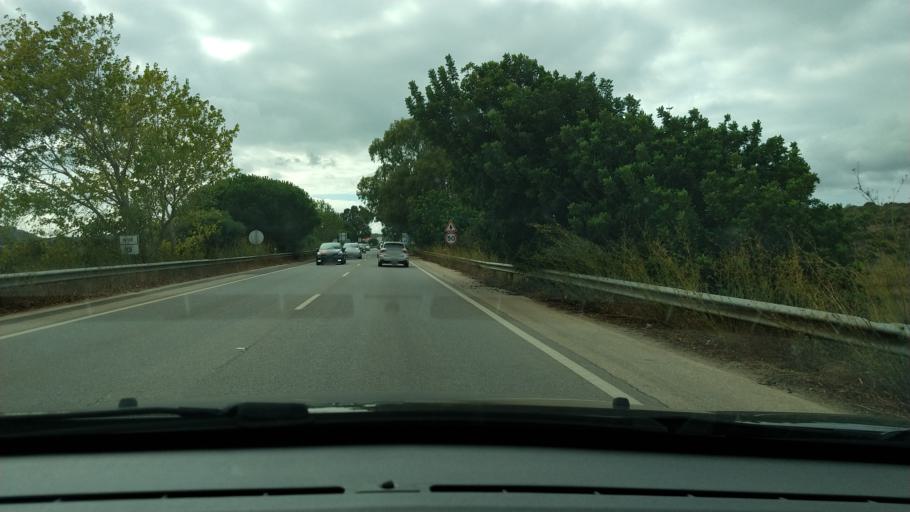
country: PT
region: Faro
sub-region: Lagos
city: Lagos
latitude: 37.0919
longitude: -8.7780
